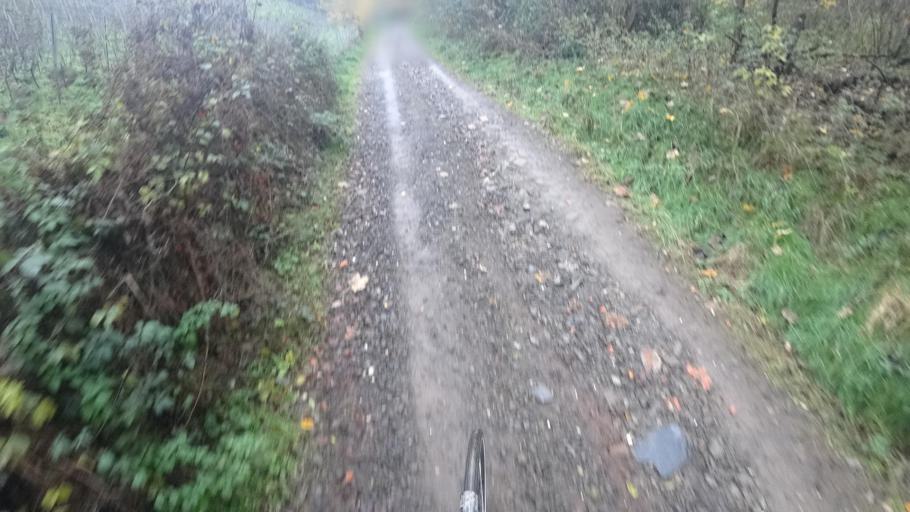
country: DE
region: Rheinland-Pfalz
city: Dernau
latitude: 50.5225
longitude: 7.0469
